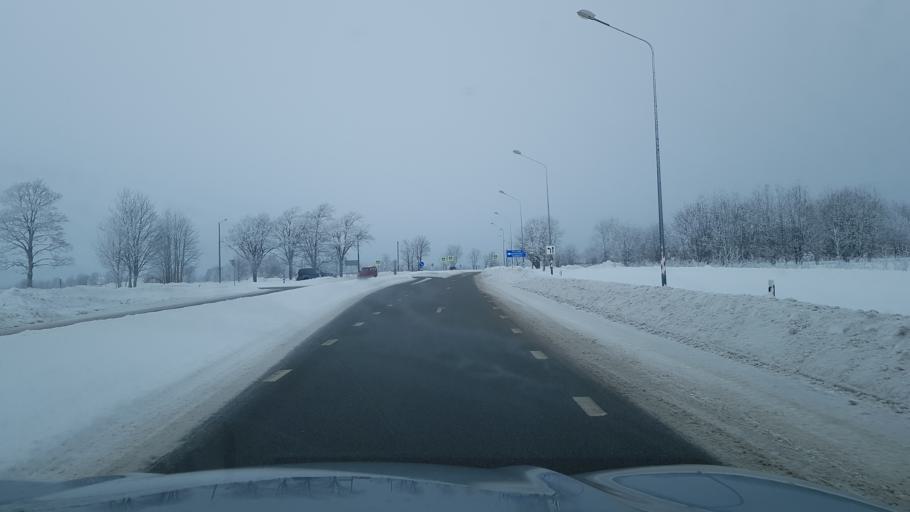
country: EE
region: Ida-Virumaa
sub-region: Johvi vald
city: Johvi
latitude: 59.3372
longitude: 27.4029
